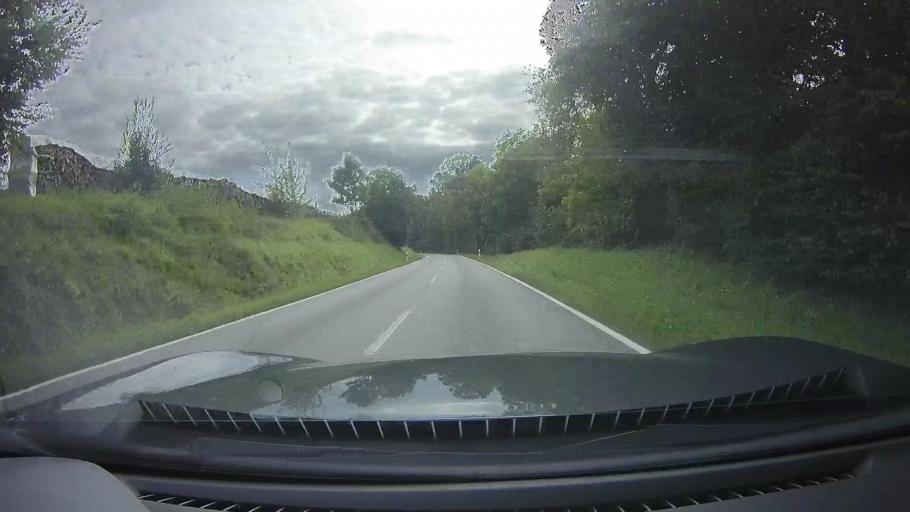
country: DE
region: Baden-Wuerttemberg
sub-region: Regierungsbezirk Stuttgart
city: Lowenstein
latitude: 49.0876
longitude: 9.3594
